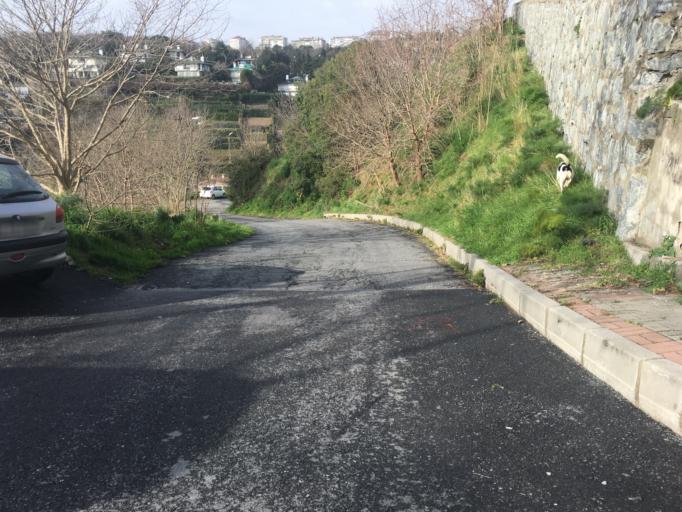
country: TR
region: Istanbul
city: UEskuedar
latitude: 41.0713
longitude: 29.0398
